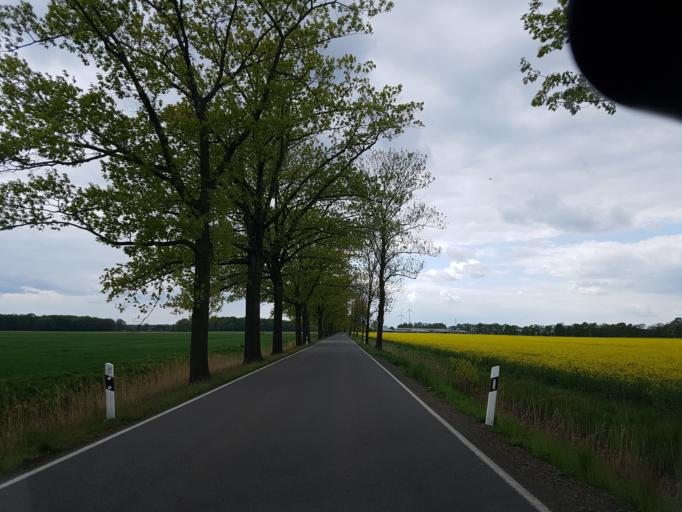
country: DE
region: Brandenburg
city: Bronkow
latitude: 51.6185
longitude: 13.9181
